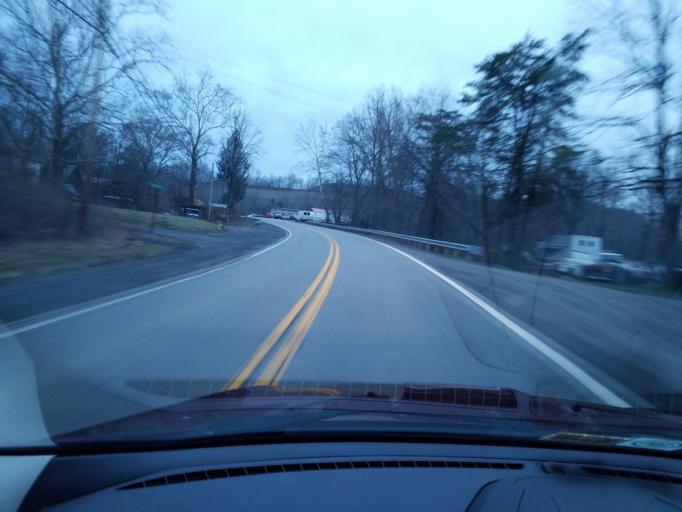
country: US
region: West Virginia
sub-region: Greenbrier County
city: Lewisburg
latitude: 37.7793
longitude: -80.3834
